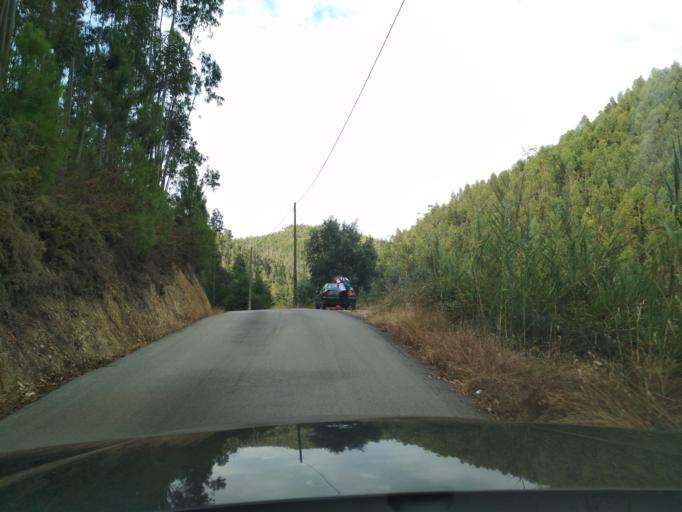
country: PT
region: Coimbra
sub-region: Coimbra
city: Coimbra
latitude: 40.2483
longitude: -8.3901
